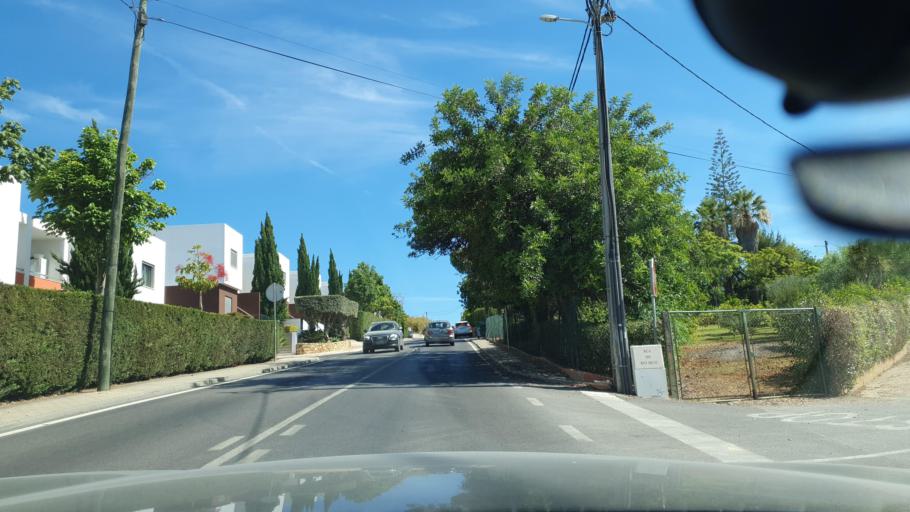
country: PT
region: Faro
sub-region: Albufeira
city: Guia
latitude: 37.0985
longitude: -8.3093
